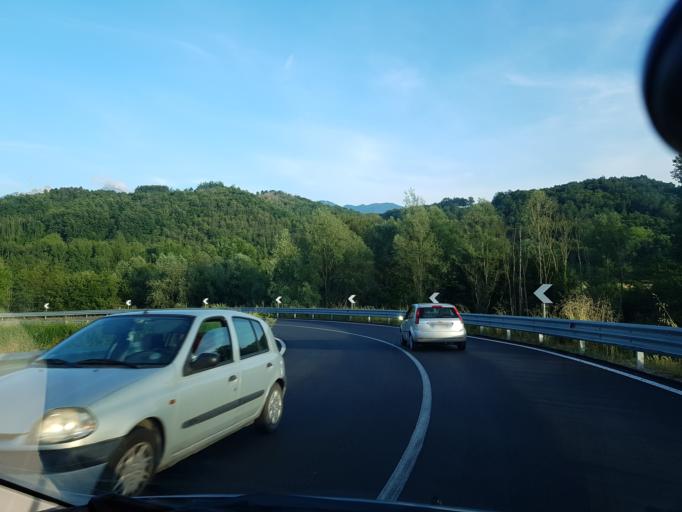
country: IT
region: Tuscany
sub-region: Provincia di Massa-Carrara
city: Fivizzano
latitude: 44.2013
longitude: 10.0873
